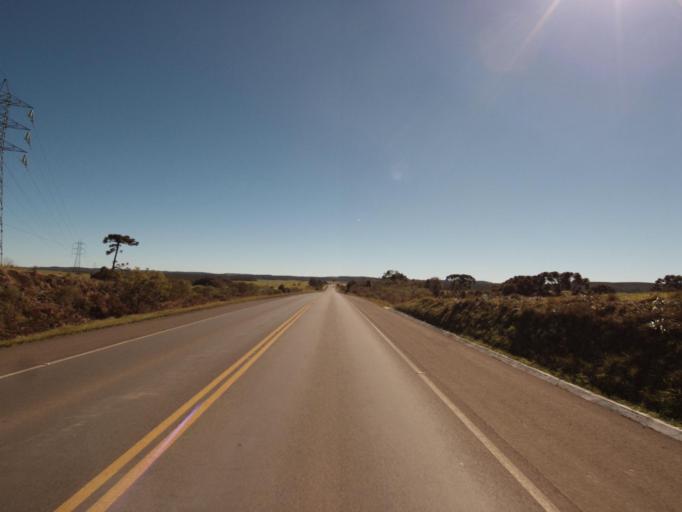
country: BR
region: Santa Catarina
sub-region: Concordia
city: Concordia
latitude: -26.9407
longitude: -51.8659
